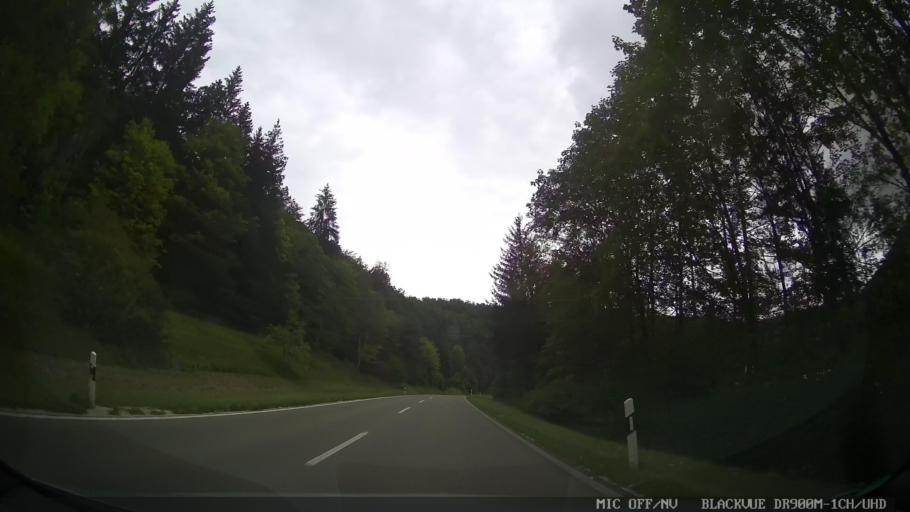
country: DE
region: Baden-Wuerttemberg
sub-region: Freiburg Region
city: Fridingen an der Donau
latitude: 48.0401
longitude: 8.9402
